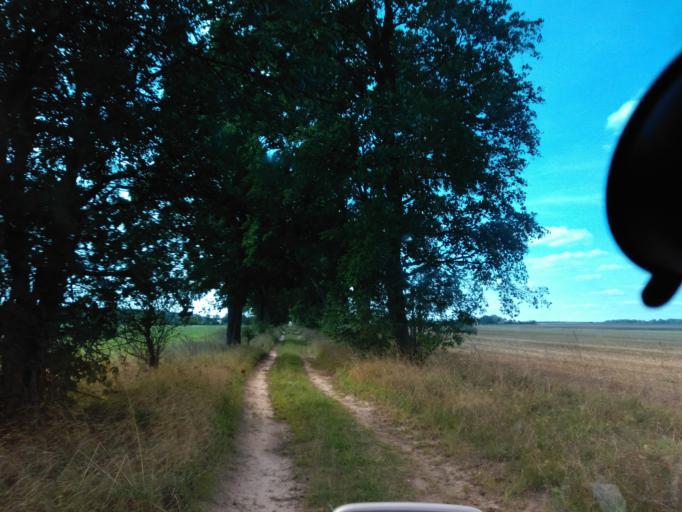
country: BY
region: Minsk
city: Stan'kava
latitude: 53.6340
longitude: 27.3240
